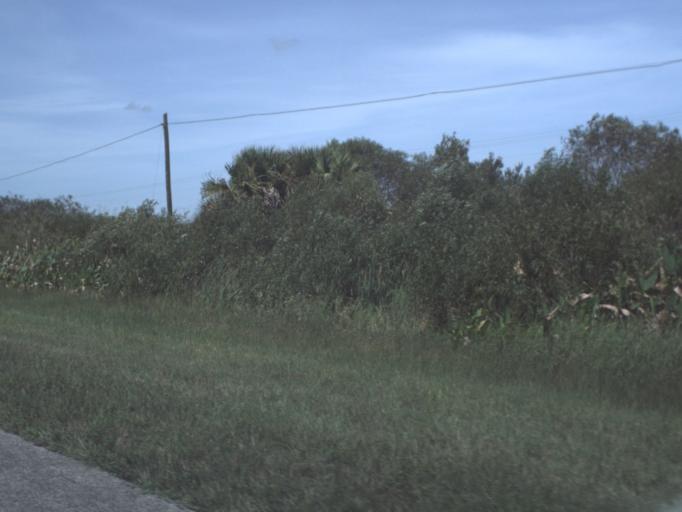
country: US
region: Florida
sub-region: Glades County
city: Moore Haven
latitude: 26.9019
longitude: -81.2503
